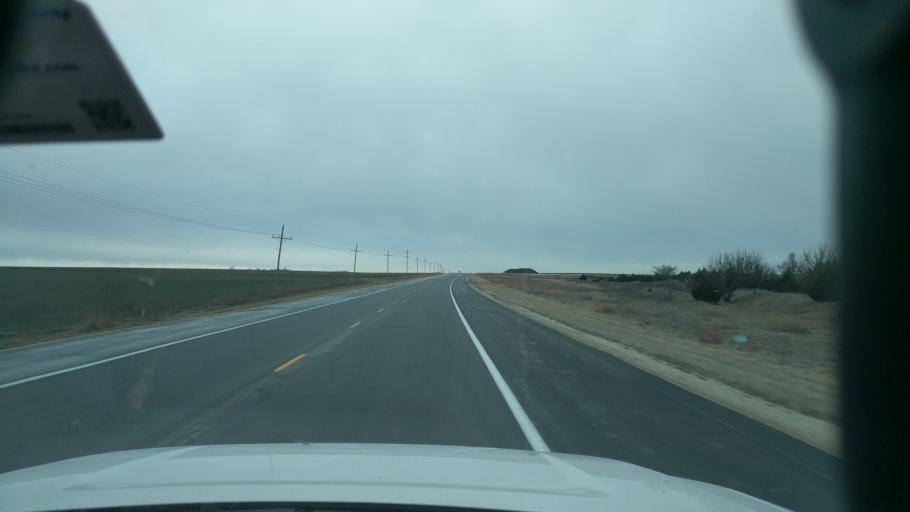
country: US
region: Kansas
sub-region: Marion County
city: Hillsboro
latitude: 38.3621
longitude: -97.2850
